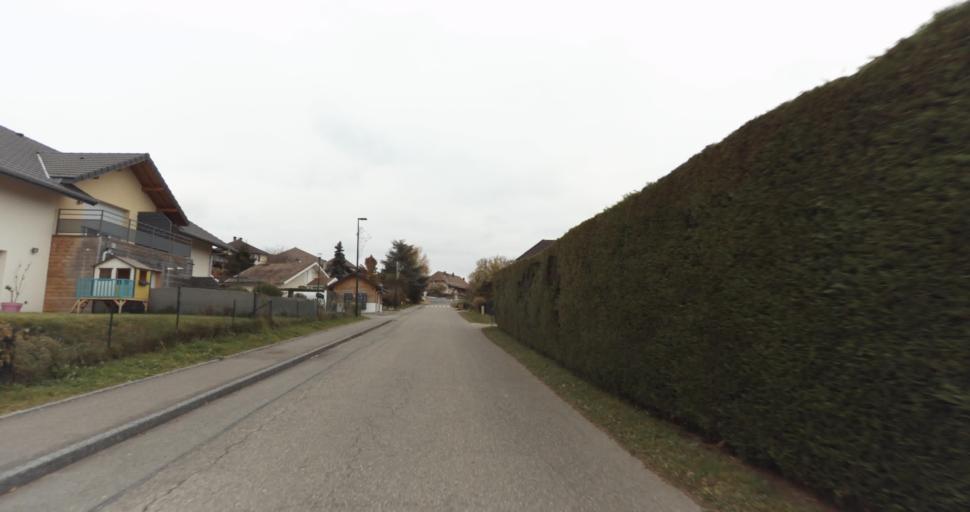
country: FR
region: Rhone-Alpes
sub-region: Departement de la Haute-Savoie
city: Chavanod
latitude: 45.8631
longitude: 6.0448
